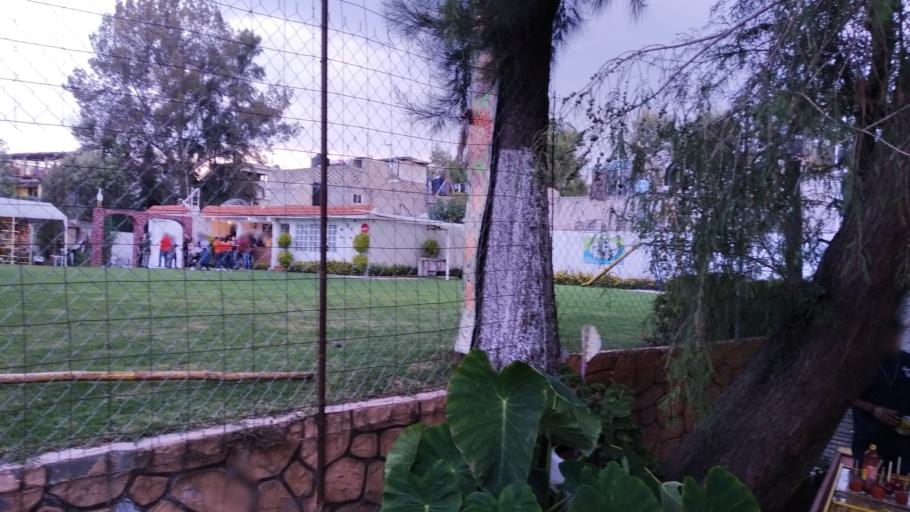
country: MX
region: Mexico City
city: Xochimilco
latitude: 19.2542
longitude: -99.0931
